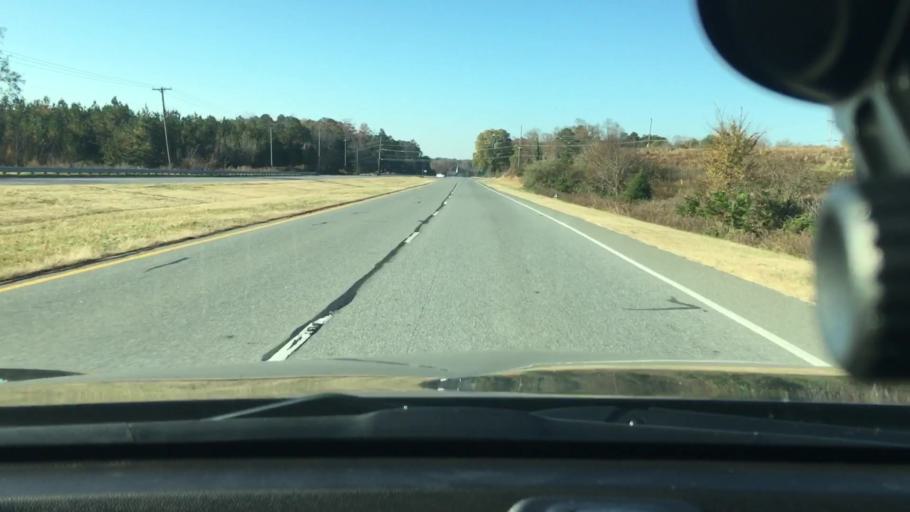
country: US
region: North Carolina
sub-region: Cabarrus County
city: Concord
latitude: 35.3828
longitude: -80.5266
